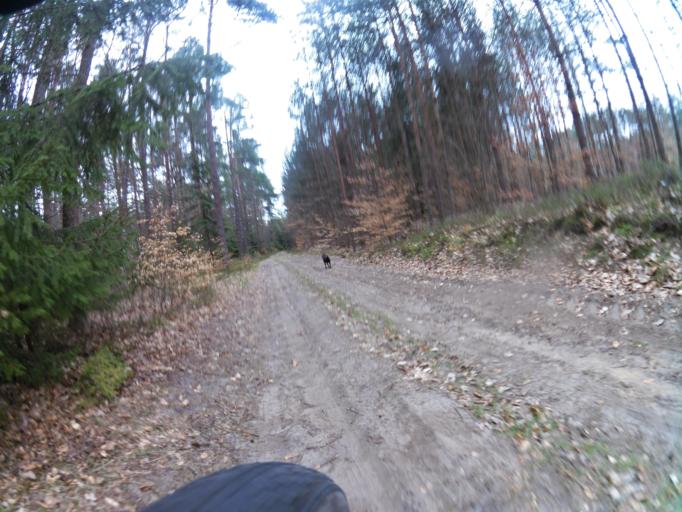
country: PL
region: West Pomeranian Voivodeship
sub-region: Powiat koszalinski
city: Polanow
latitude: 54.1681
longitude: 16.6460
